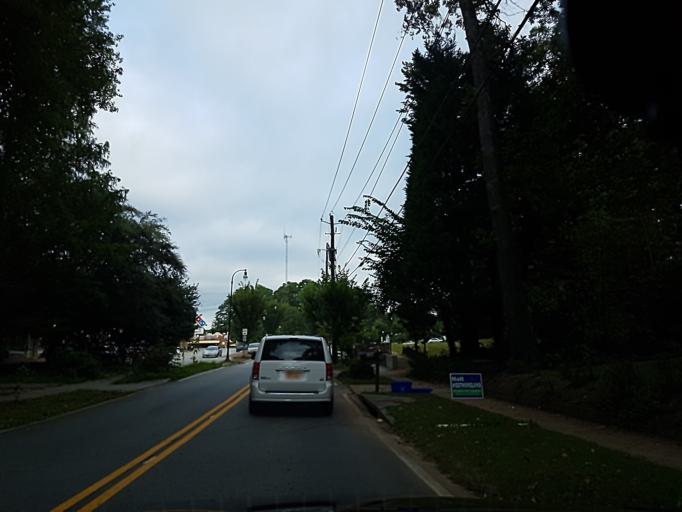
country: US
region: Georgia
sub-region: DeKalb County
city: Druid Hills
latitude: 33.7870
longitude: -84.3245
